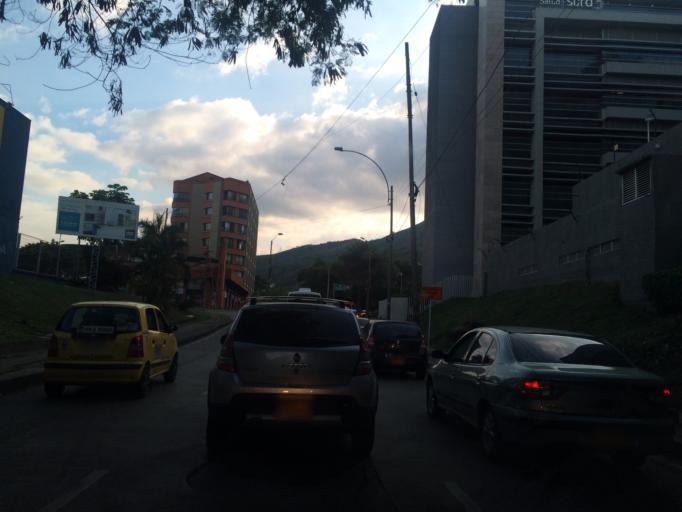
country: CO
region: Valle del Cauca
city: Cali
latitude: 3.4739
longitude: -76.5268
